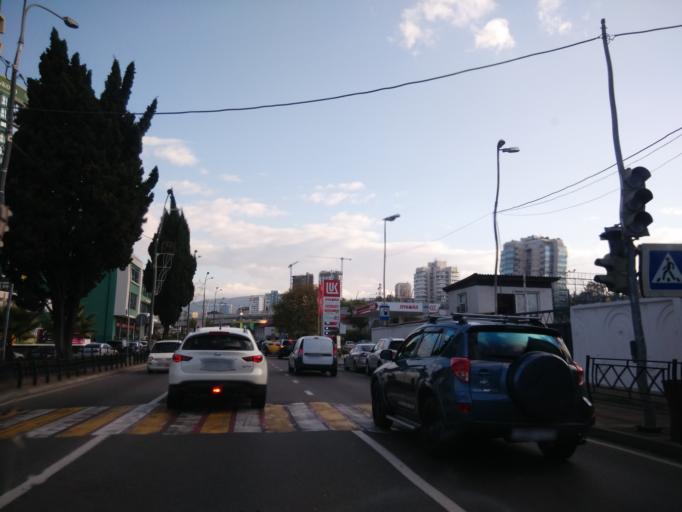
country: RU
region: Krasnodarskiy
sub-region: Sochi City
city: Sochi
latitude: 43.5946
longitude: 39.7291
